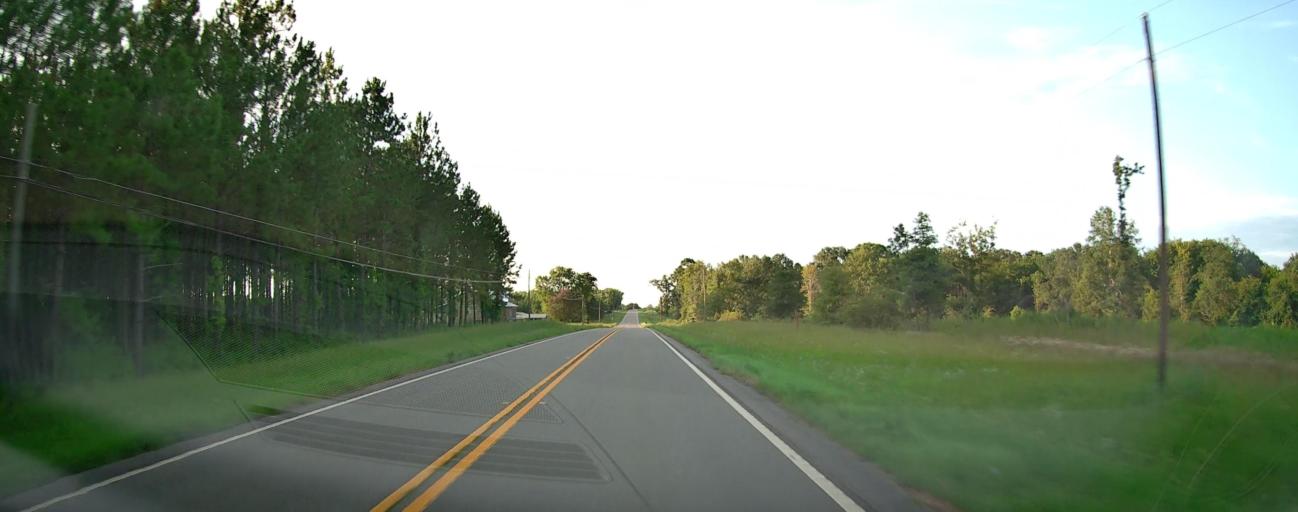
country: US
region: Georgia
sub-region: Taylor County
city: Reynolds
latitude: 32.5806
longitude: -84.0897
